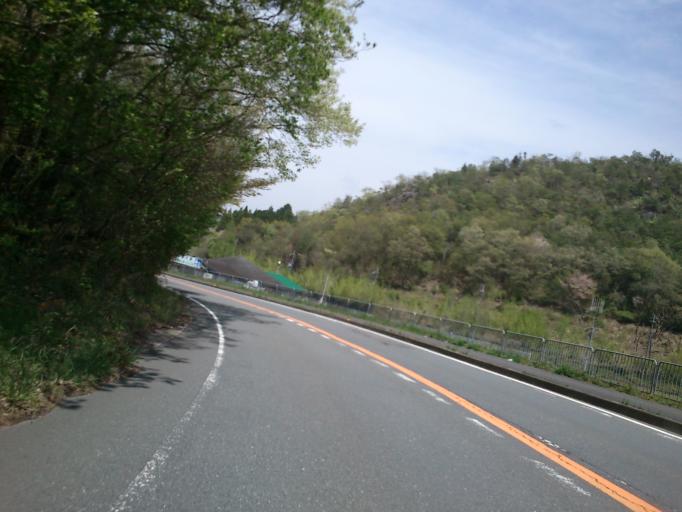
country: JP
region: Kyoto
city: Ayabe
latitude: 35.1659
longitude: 135.3615
